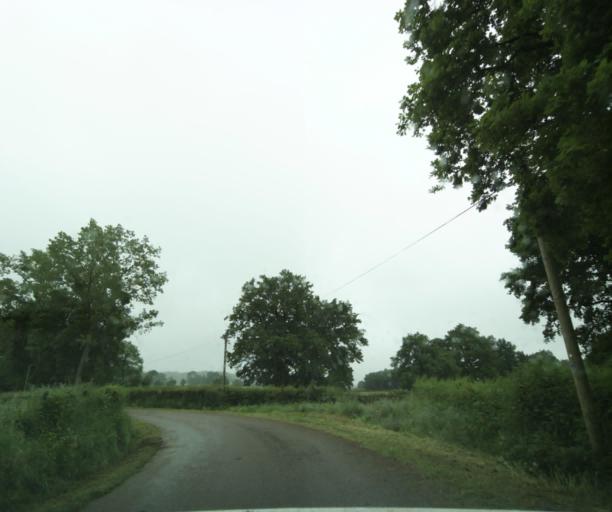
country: FR
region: Bourgogne
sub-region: Departement de Saone-et-Loire
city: Charolles
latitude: 46.4254
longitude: 4.3389
